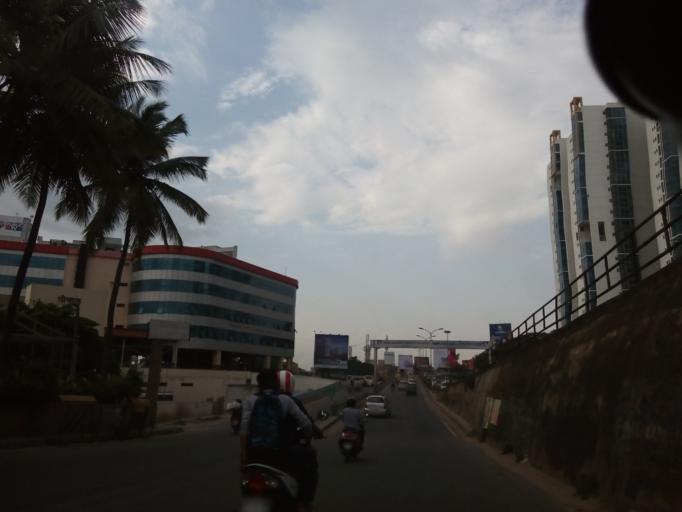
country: IN
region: Karnataka
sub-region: Bangalore Urban
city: Bangalore
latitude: 13.0165
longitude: 77.5564
